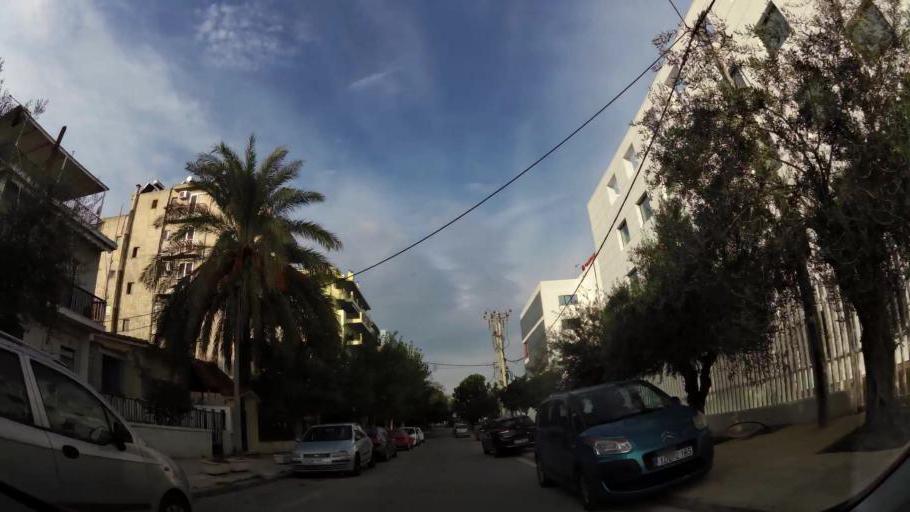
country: GR
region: Attica
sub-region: Nomarchia Athinas
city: Palaio Faliro
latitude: 37.9376
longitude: 23.6968
